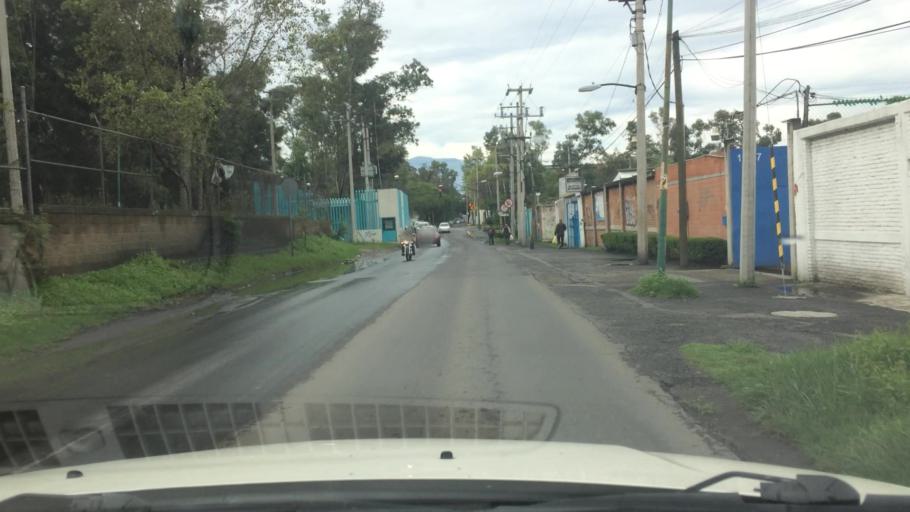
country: MX
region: Mexico City
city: Xochimilco
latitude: 19.3012
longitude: -99.1008
